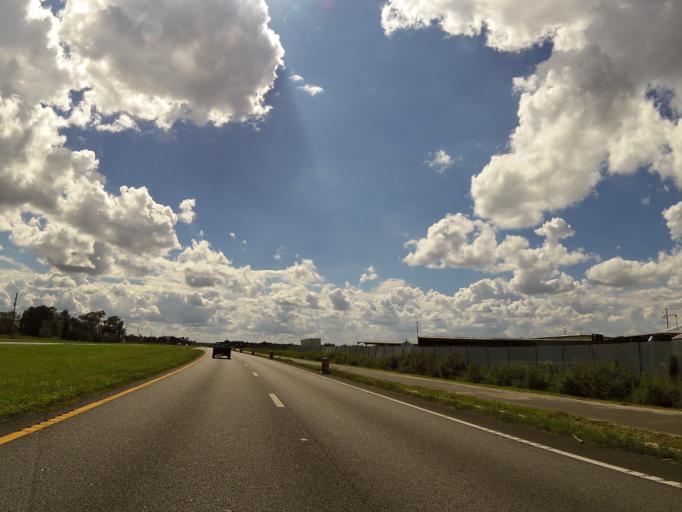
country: US
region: Florida
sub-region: Putnam County
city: East Palatka
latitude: 29.7136
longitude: -81.5218
